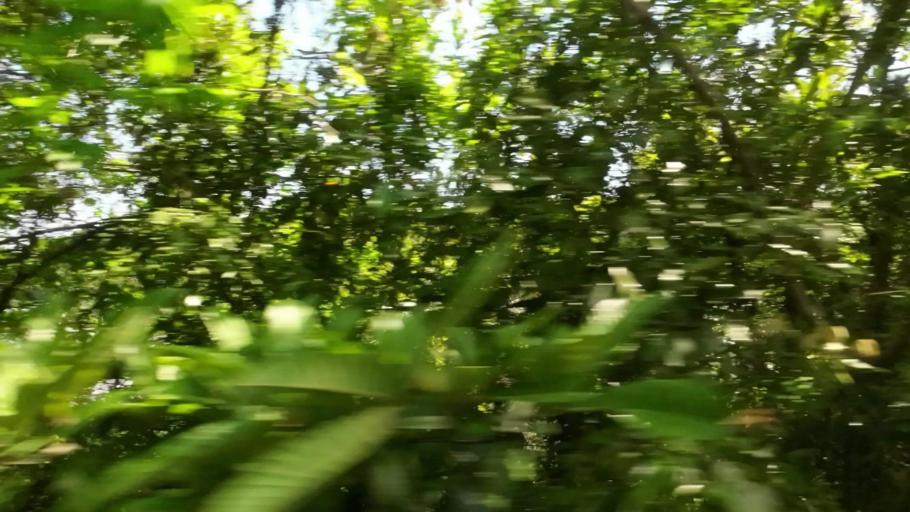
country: JP
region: Ehime
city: Niihama
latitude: 33.9701
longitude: 133.3565
